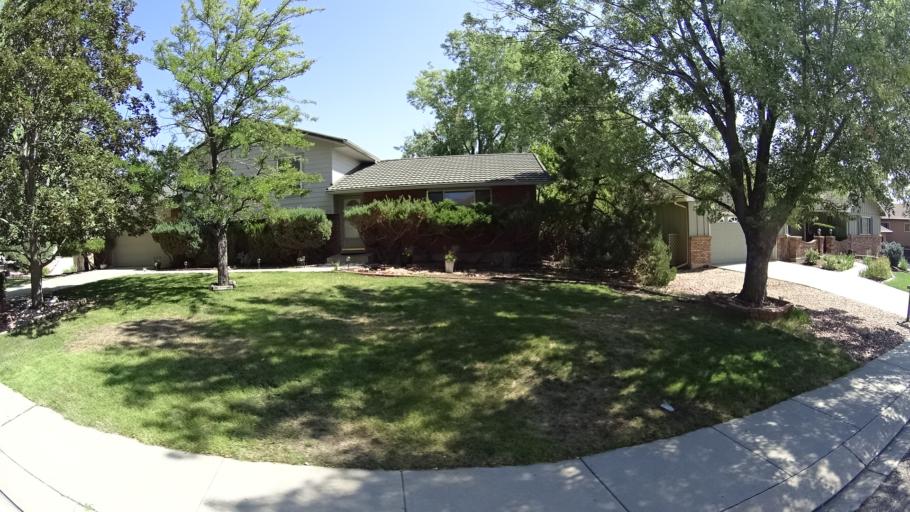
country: US
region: Colorado
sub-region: El Paso County
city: Air Force Academy
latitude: 38.9216
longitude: -104.8241
